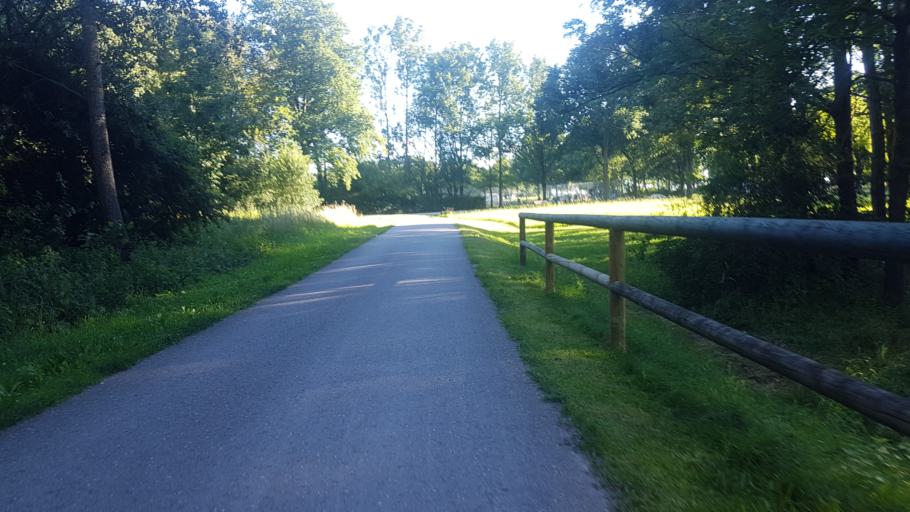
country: DE
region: Bavaria
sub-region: Regierungsbezirk Mittelfranken
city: Absberg
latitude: 49.1408
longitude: 10.8730
